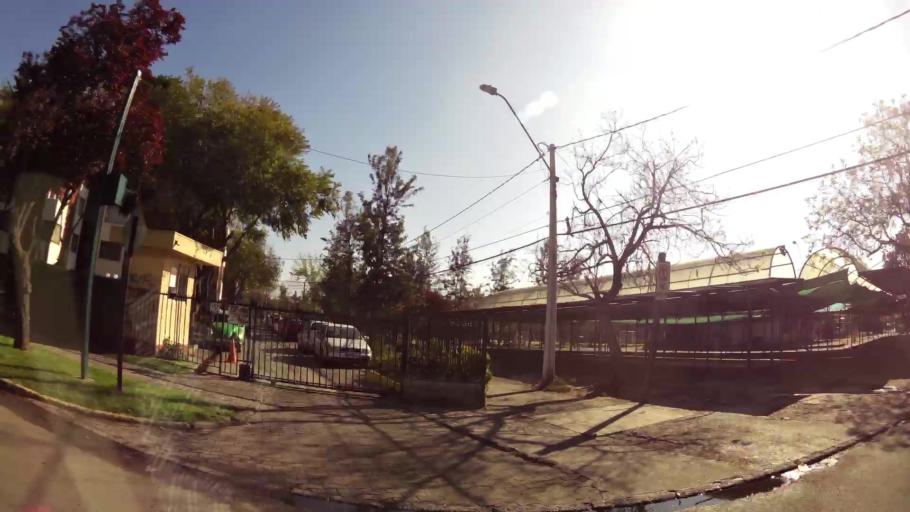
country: CL
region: Santiago Metropolitan
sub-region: Provincia de Santiago
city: Villa Presidente Frei, Nunoa, Santiago, Chile
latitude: -33.4422
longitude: -70.5794
